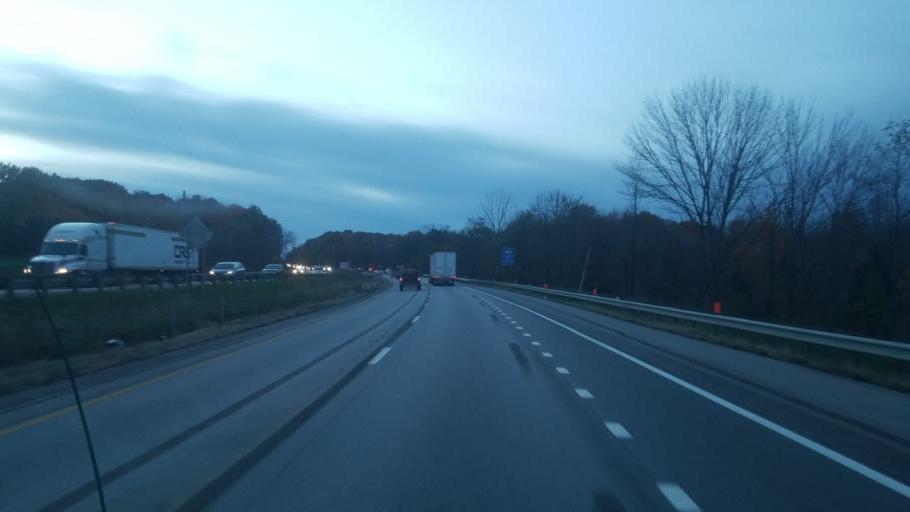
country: US
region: Ohio
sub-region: Medina County
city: Wadsworth
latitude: 41.0472
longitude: -81.6973
